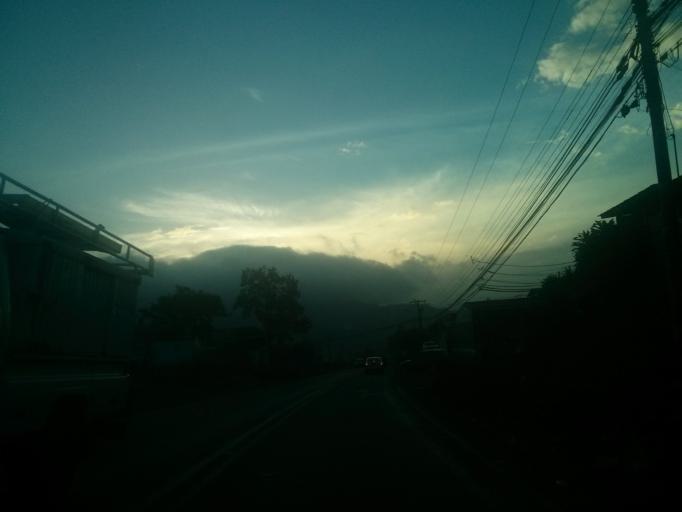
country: CR
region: Cartago
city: Cartago
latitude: 9.8772
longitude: -83.9272
